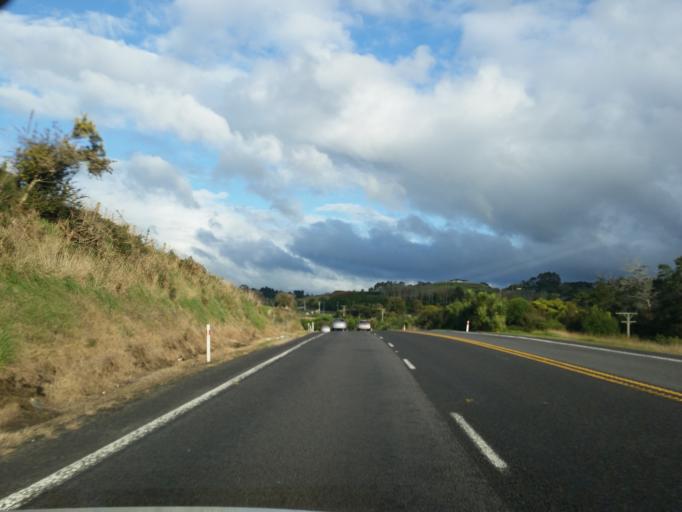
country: NZ
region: Bay of Plenty
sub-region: Western Bay of Plenty District
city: Katikati
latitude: -37.6445
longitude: 175.9648
